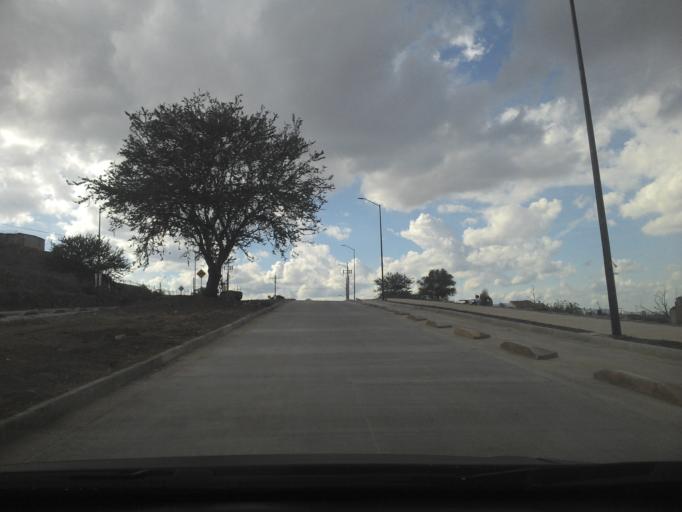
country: MX
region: Jalisco
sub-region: Tlajomulco de Zuniga
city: Altus Bosques
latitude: 20.6155
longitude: -103.3661
